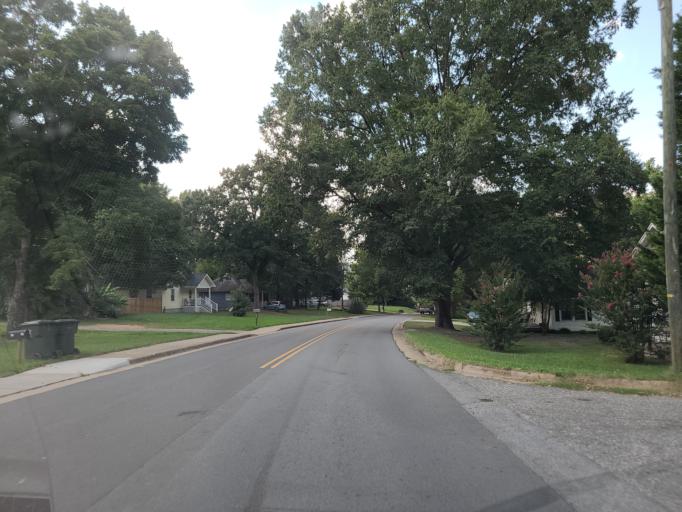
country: US
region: North Carolina
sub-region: Gaston County
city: Lowell
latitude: 35.2798
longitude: -81.0992
